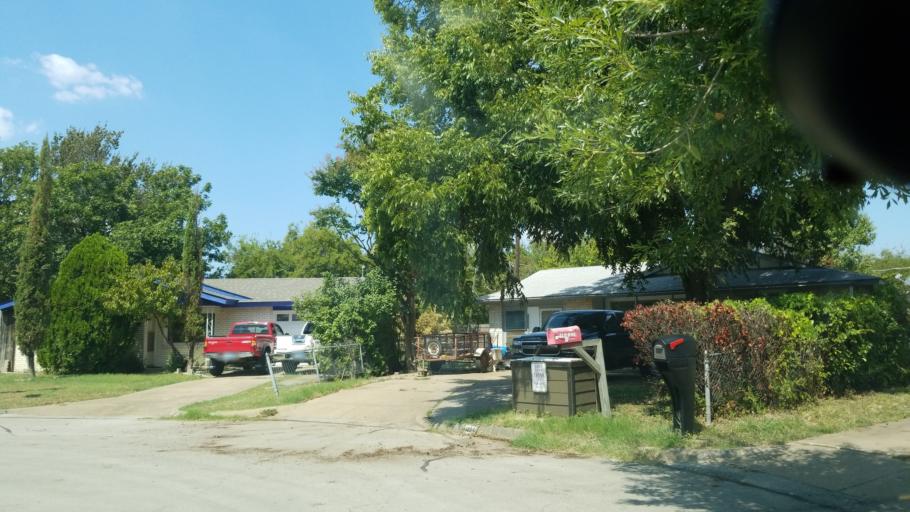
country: US
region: Texas
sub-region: Dallas County
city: Grand Prairie
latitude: 32.7114
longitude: -96.9864
